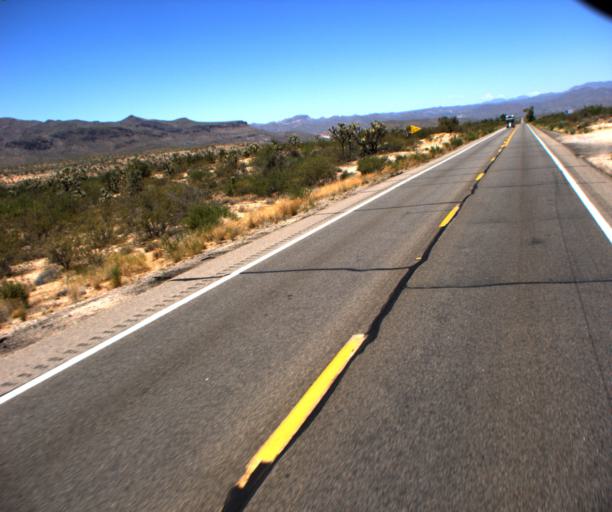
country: US
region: Arizona
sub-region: Yavapai County
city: Bagdad
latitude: 34.2981
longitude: -113.1166
